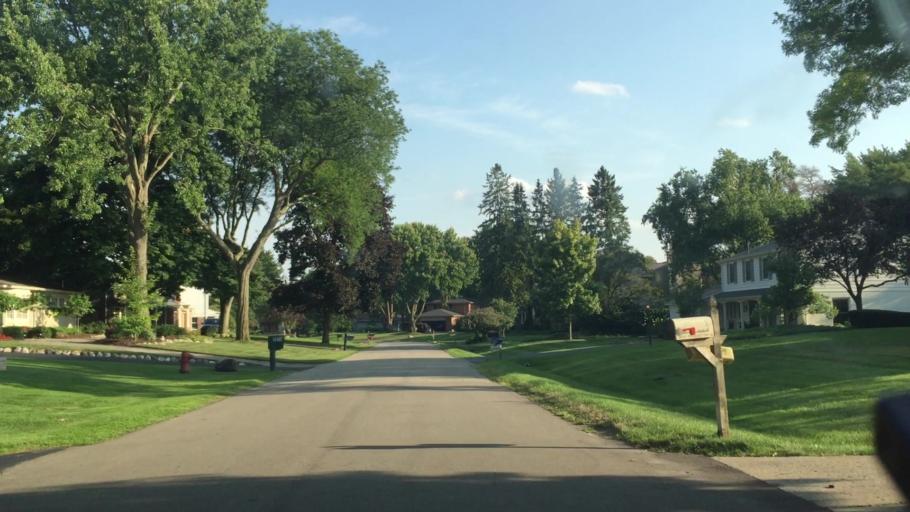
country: US
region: Michigan
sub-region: Oakland County
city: Bloomfield Hills
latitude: 42.5580
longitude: -83.2717
